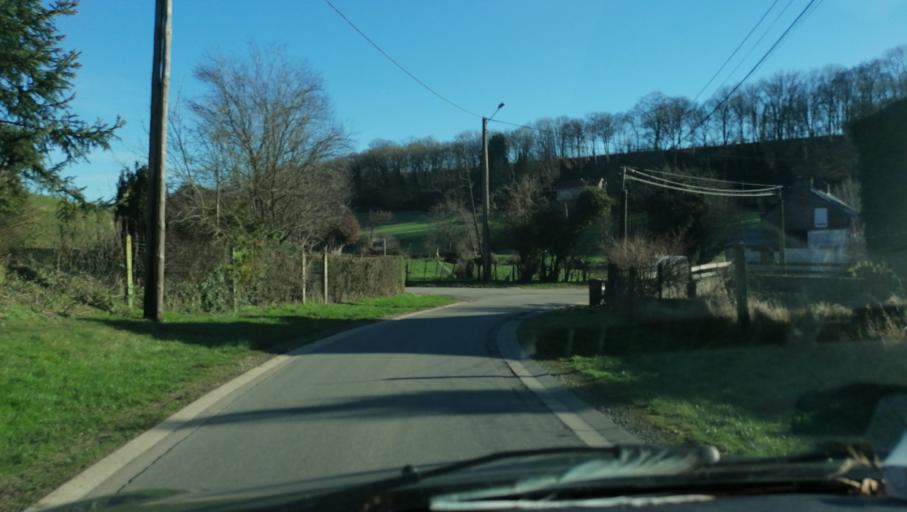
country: FR
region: Nord-Pas-de-Calais
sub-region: Departement du Nord
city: Marpent
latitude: 50.2057
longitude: 4.0751
